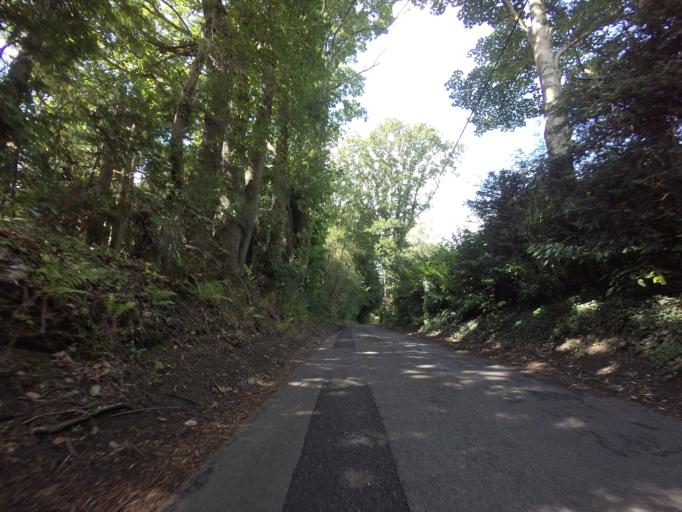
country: GB
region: England
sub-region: Kent
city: Borough Green
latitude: 51.2747
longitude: 0.2760
